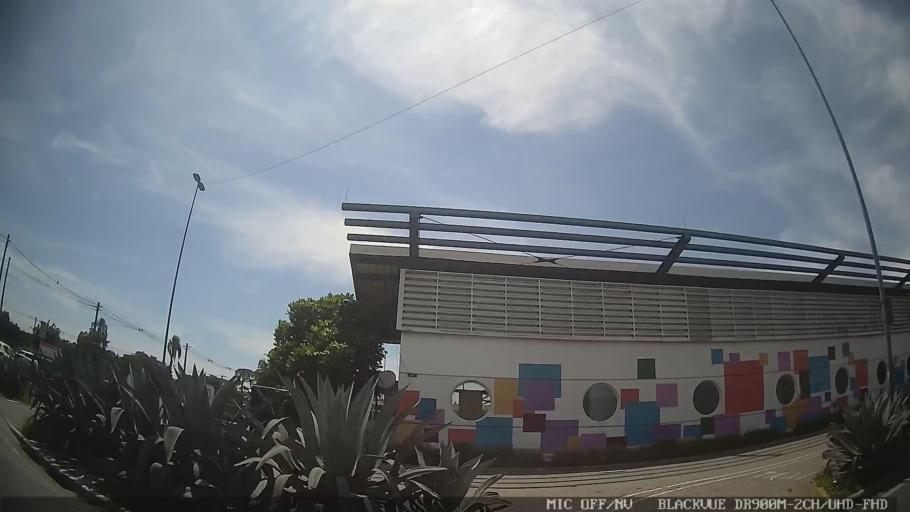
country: BR
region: Sao Paulo
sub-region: Suzano
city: Suzano
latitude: -23.5336
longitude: -46.3075
